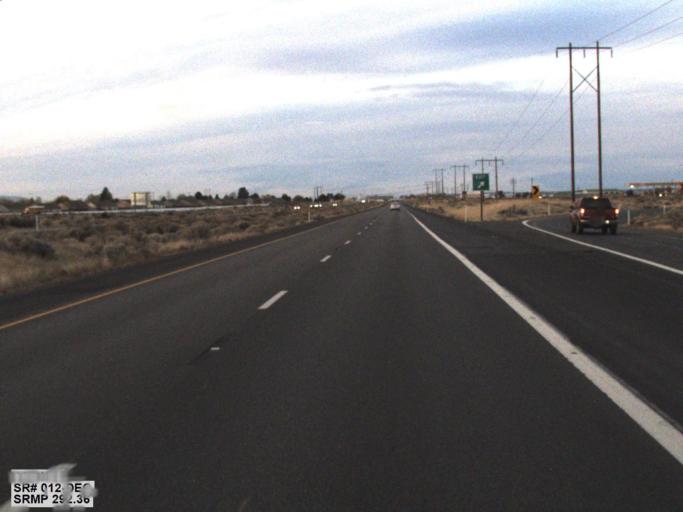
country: US
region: Washington
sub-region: Franklin County
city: Pasco
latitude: 46.2399
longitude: -119.0572
